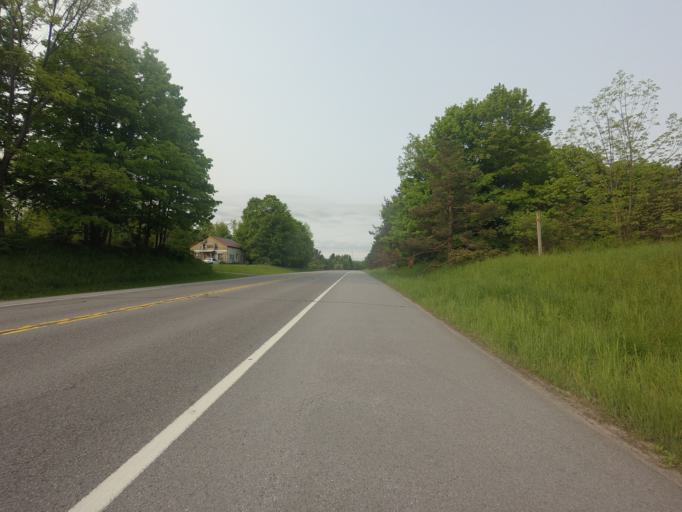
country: US
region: New York
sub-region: Jefferson County
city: Carthage
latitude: 44.0459
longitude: -75.5632
